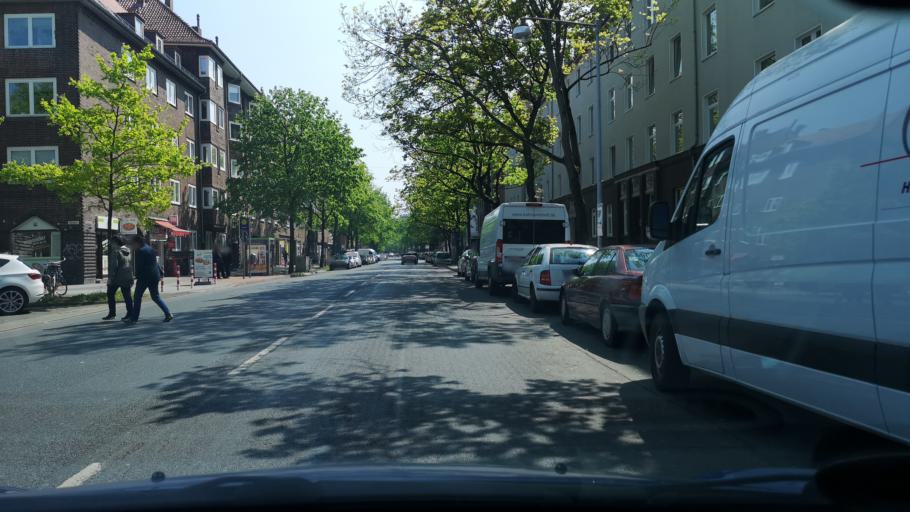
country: DE
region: Lower Saxony
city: Hannover
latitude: 52.3942
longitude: 9.7287
